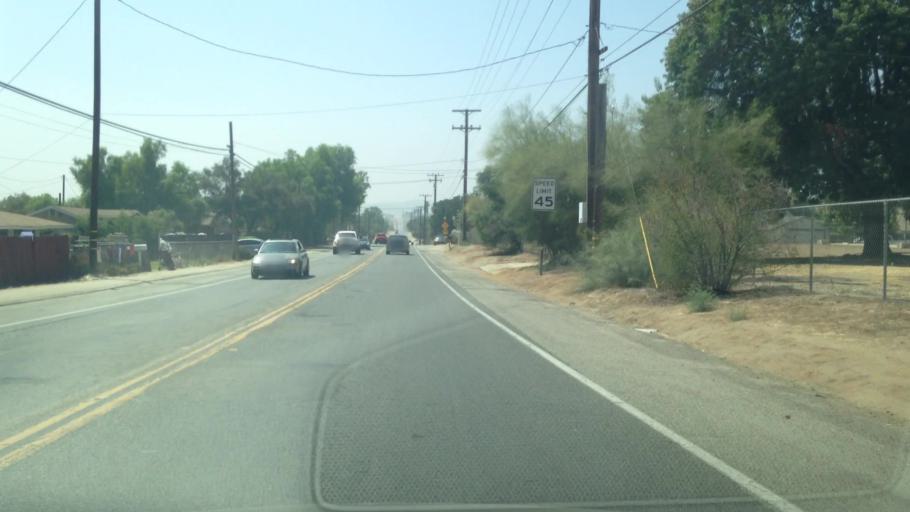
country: US
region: California
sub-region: Riverside County
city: Woodcrest
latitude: 33.8725
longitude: -117.3314
